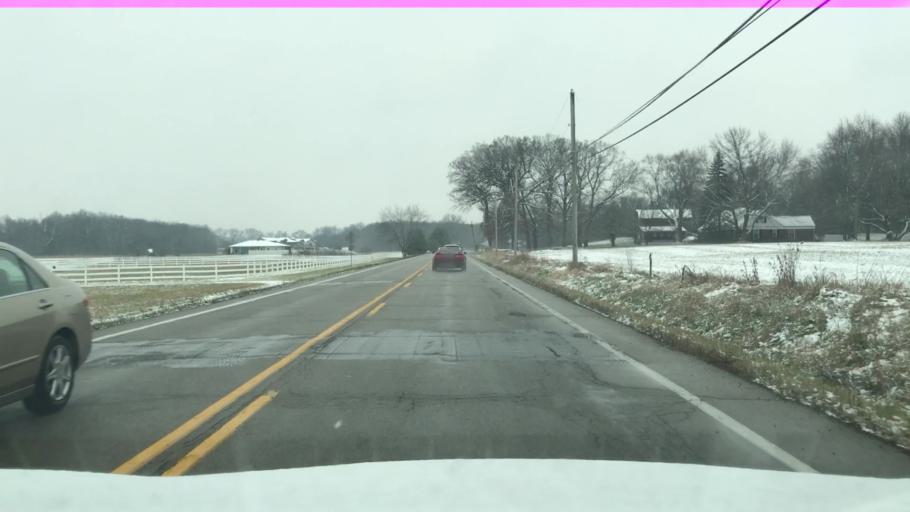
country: US
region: Indiana
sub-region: Delaware County
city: Yorktown
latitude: 40.1596
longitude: -85.5311
